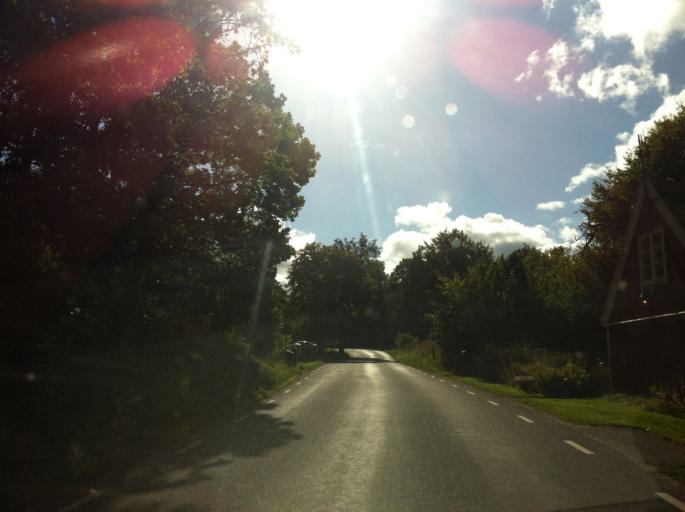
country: SE
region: Skane
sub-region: Kristianstads Kommun
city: Degeberga
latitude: 55.7170
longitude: 13.9709
